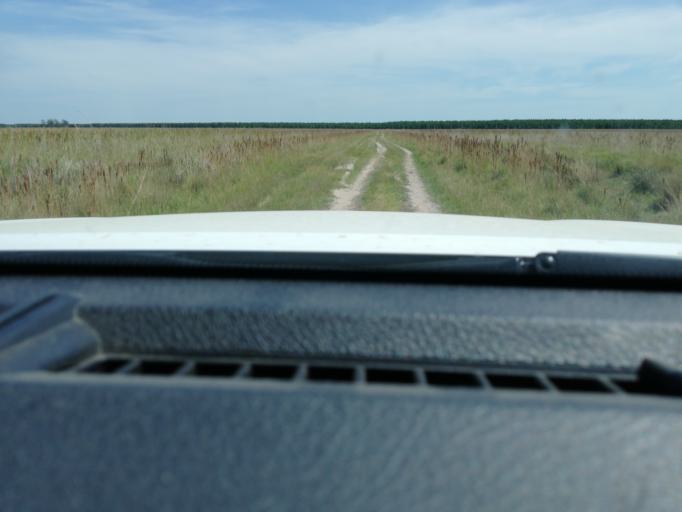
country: AR
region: Corrientes
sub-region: Departamento de San Miguel
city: San Miguel
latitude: -28.0486
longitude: -57.4556
